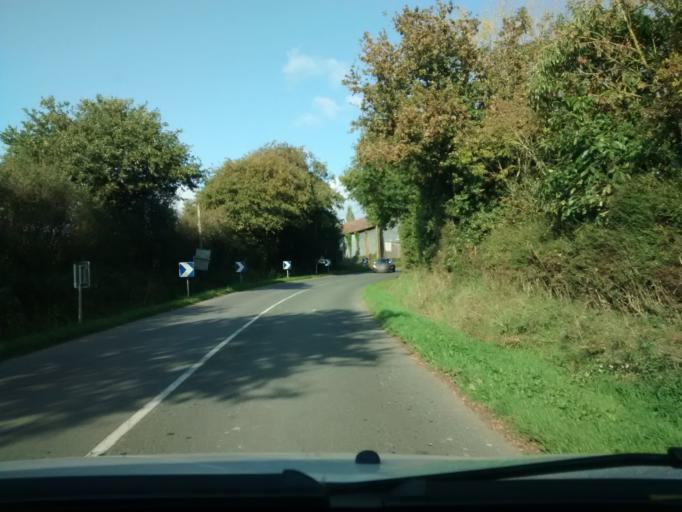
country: FR
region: Pays de la Loire
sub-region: Departement de la Loire-Atlantique
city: Coueron
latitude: 47.2380
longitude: -1.7001
